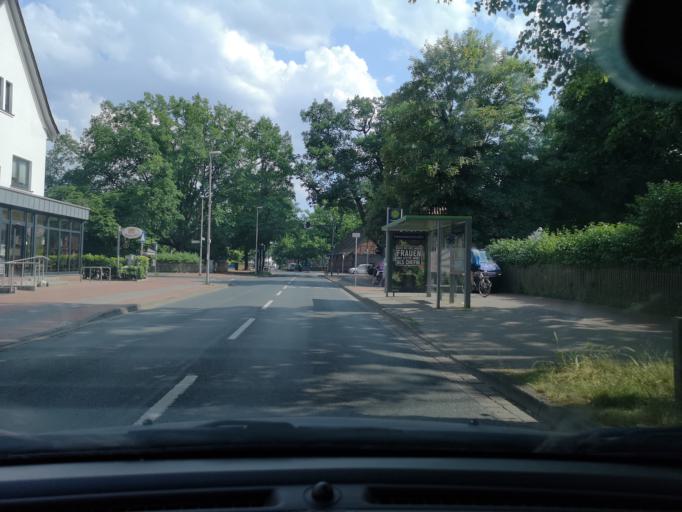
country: DE
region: Lower Saxony
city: Hannover
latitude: 52.4018
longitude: 9.8025
